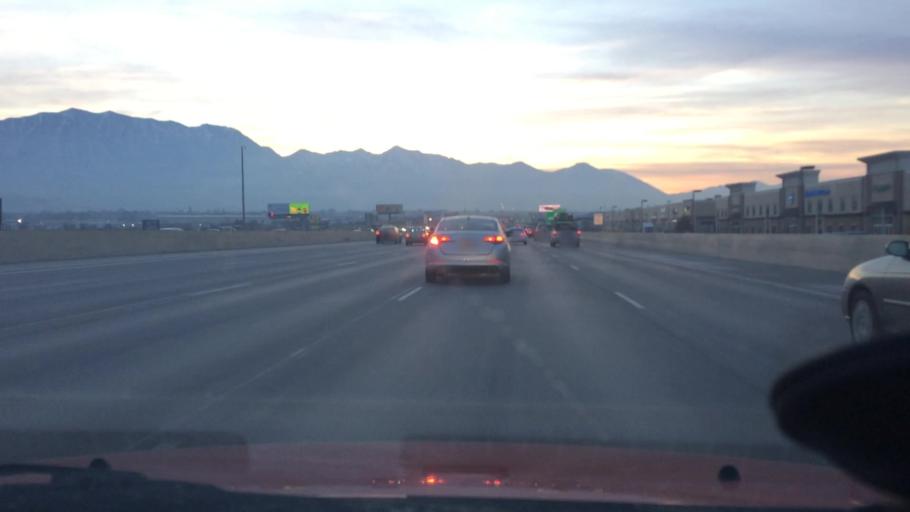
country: US
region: Utah
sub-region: Utah County
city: Pleasant Grove
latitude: 40.3397
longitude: -111.7533
